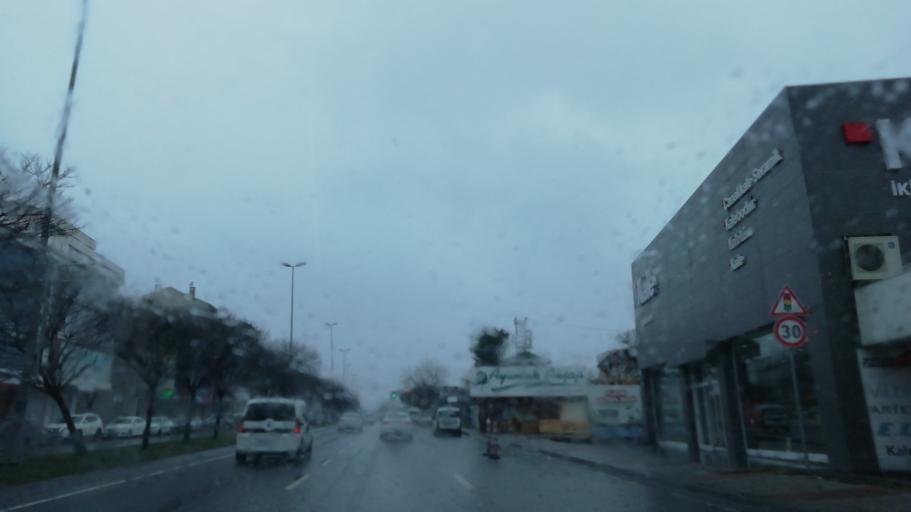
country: TR
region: Istanbul
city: Yakuplu
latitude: 41.0017
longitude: 28.7112
